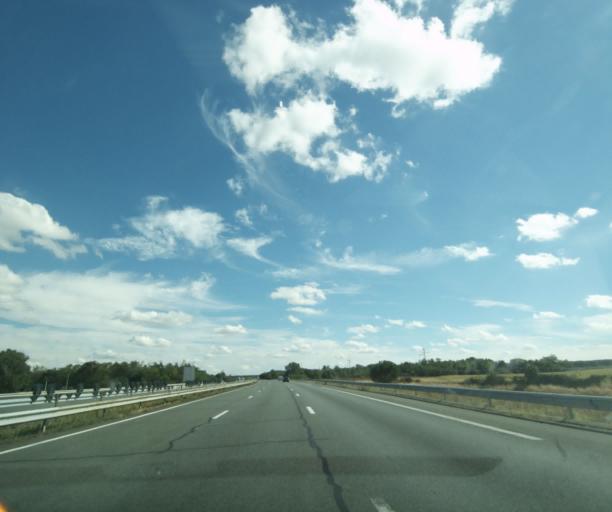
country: FR
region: Midi-Pyrenees
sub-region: Departement du Tarn-et-Garonne
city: Pompignan
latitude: 43.8435
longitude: 1.3252
